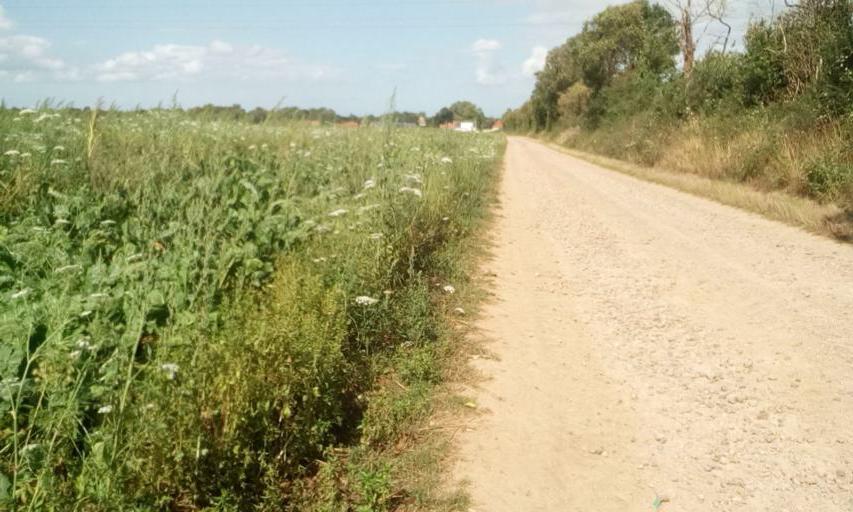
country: FR
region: Lower Normandy
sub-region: Departement du Calvados
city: Bellengreville
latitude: 49.1052
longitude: -0.2264
